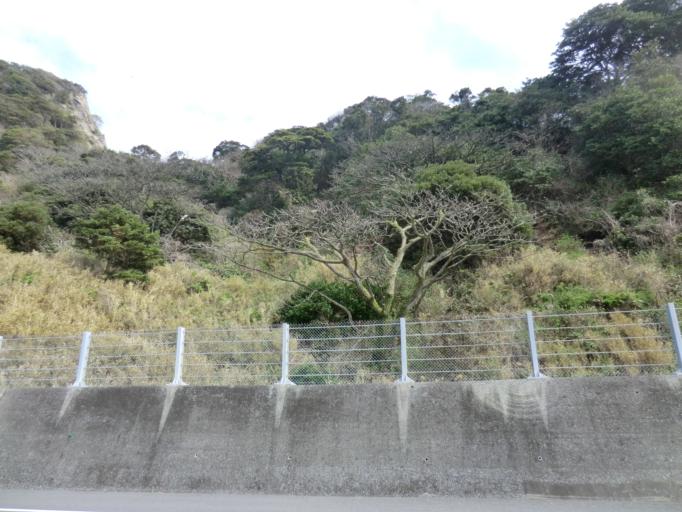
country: JP
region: Chiba
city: Futtsu
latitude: 35.1586
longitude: 139.8196
